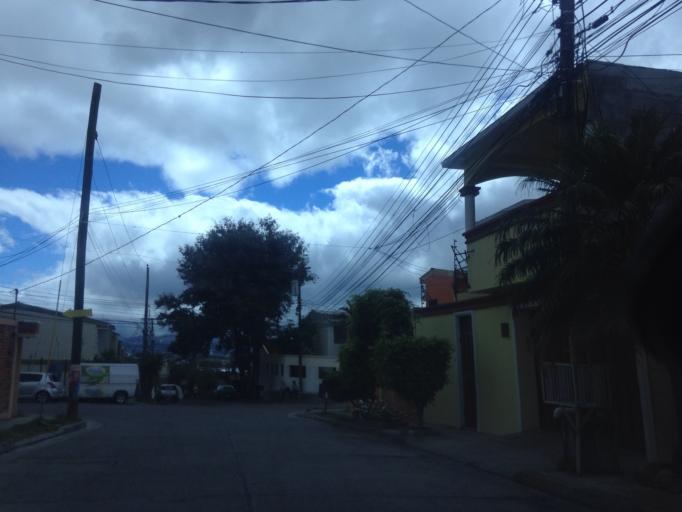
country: HN
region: Francisco Morazan
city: Tegucigalpa
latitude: 14.0553
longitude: -87.2370
